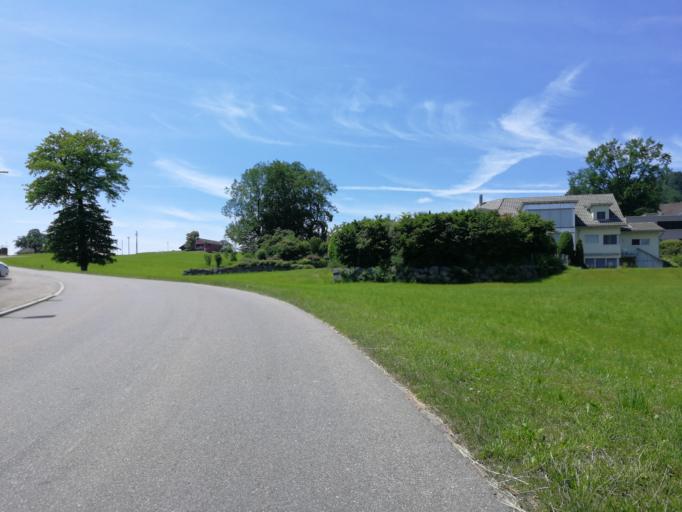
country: CH
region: Schwyz
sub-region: Bezirk March
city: Tuggen
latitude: 47.2026
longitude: 8.9356
